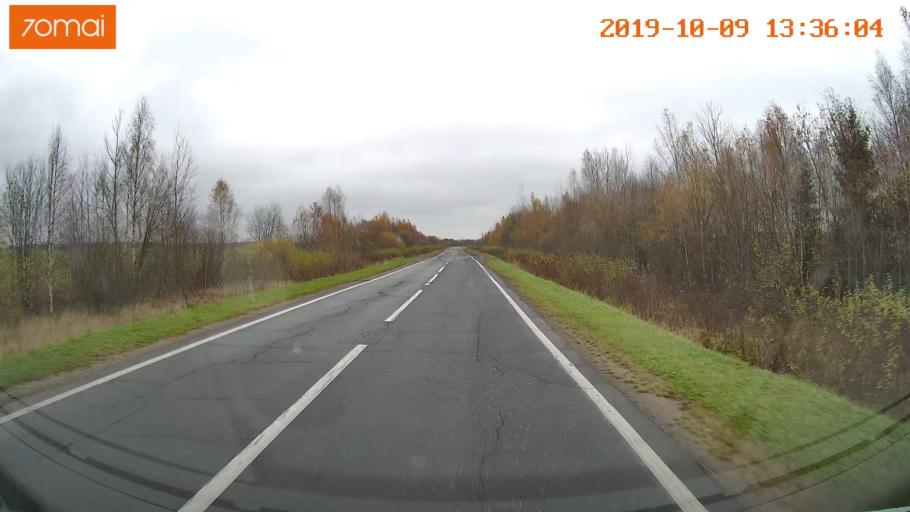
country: RU
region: Jaroslavl
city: Lyubim
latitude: 58.3390
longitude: 41.0908
